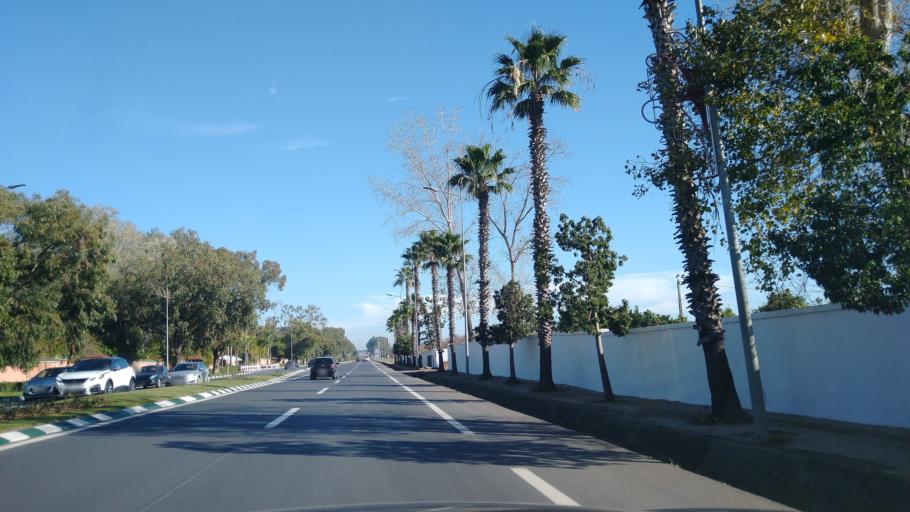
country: MA
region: Rabat-Sale-Zemmour-Zaer
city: Sale
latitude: 34.0299
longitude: -6.7445
